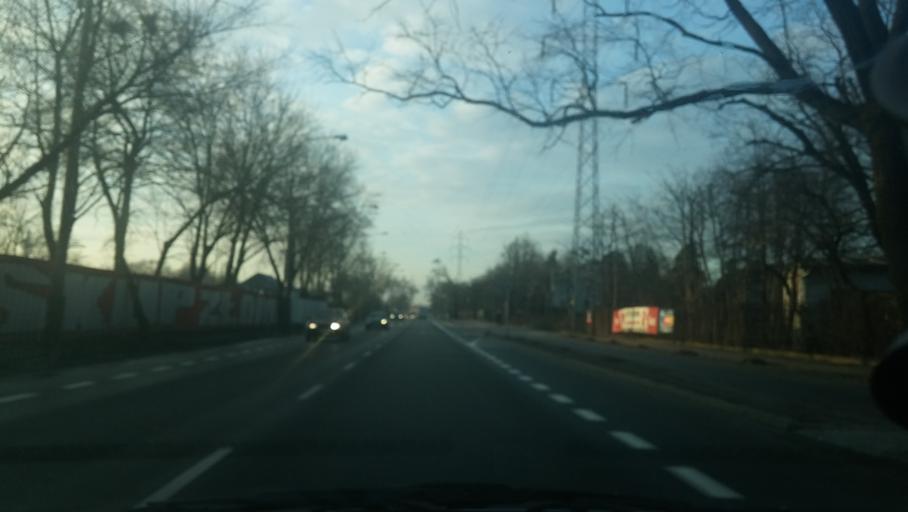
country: PL
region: Masovian Voivodeship
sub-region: Warszawa
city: Wawer
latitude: 52.2218
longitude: 21.1522
